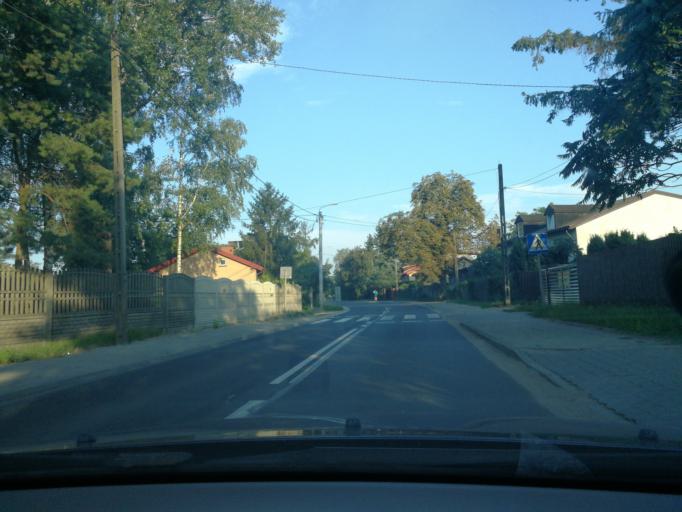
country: PL
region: Masovian Voivodeship
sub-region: Powiat warszawski zachodni
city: Ozarow Mazowiecki
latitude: 52.1901
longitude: 20.7554
